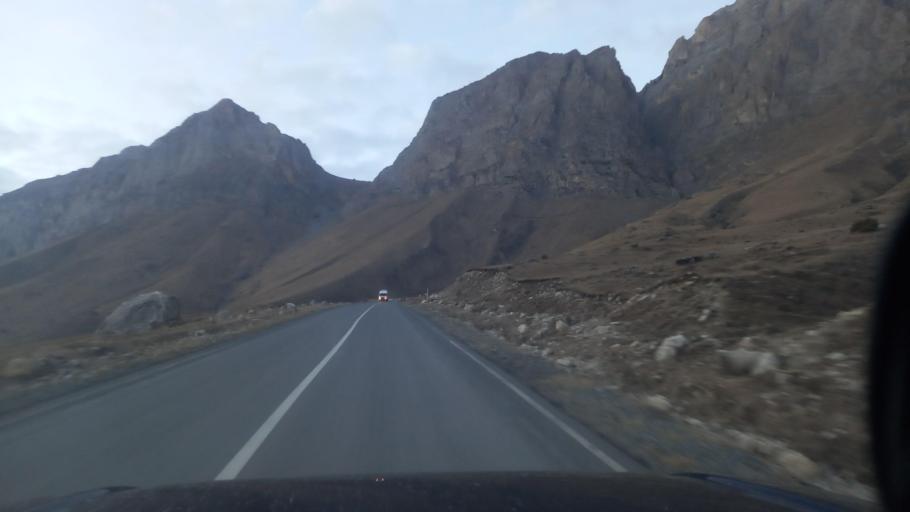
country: RU
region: Ingushetiya
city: Dzhayrakh
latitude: 42.8223
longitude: 44.8259
